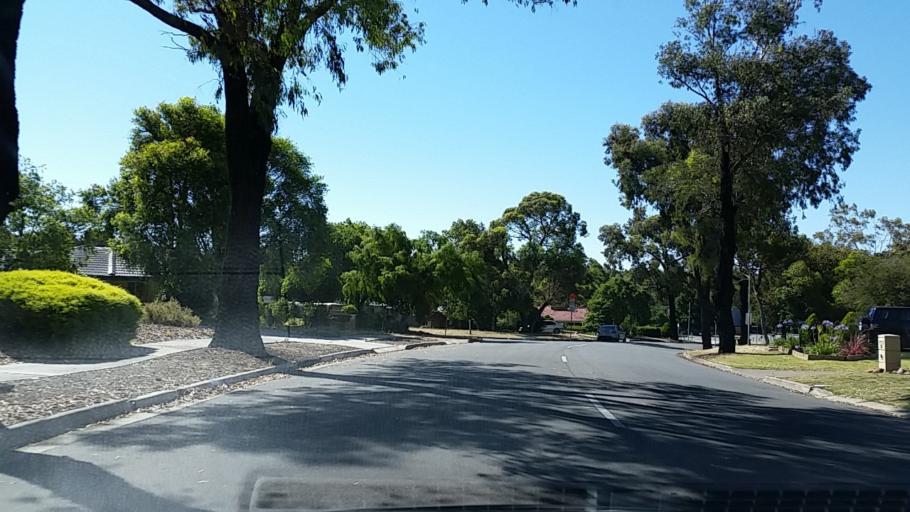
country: AU
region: South Australia
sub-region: Tea Tree Gully
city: Hope Valley
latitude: -34.8034
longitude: 138.7018
